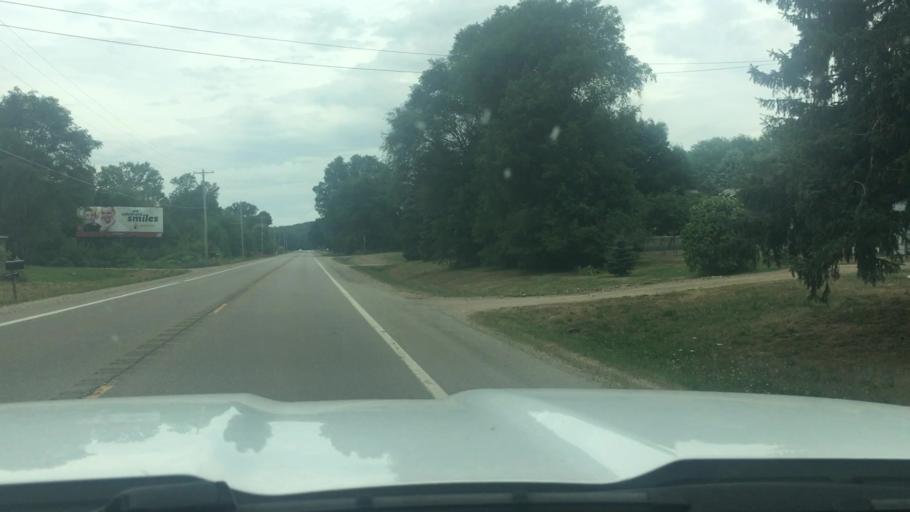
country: US
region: Michigan
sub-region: Kent County
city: Lowell
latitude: 42.9371
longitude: -85.2965
